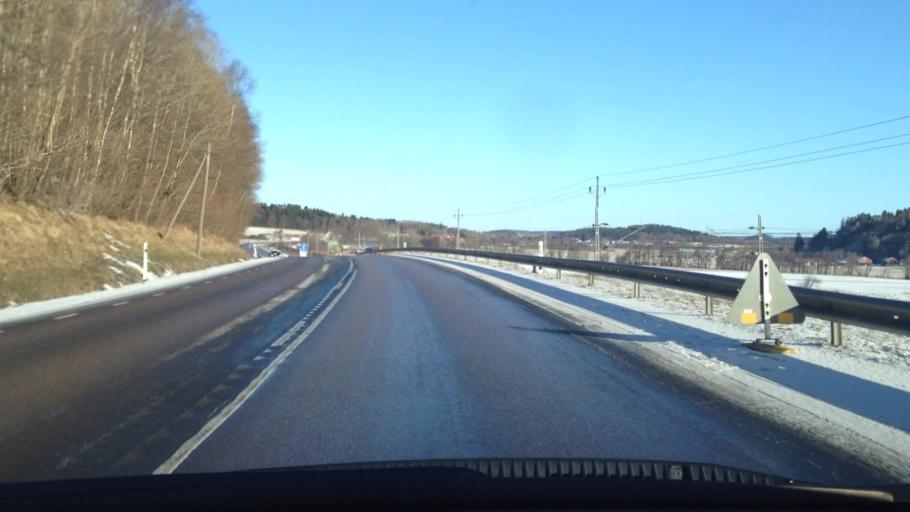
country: SE
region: Vaestra Goetaland
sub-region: Molndal
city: Lindome
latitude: 57.5519
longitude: 12.0927
